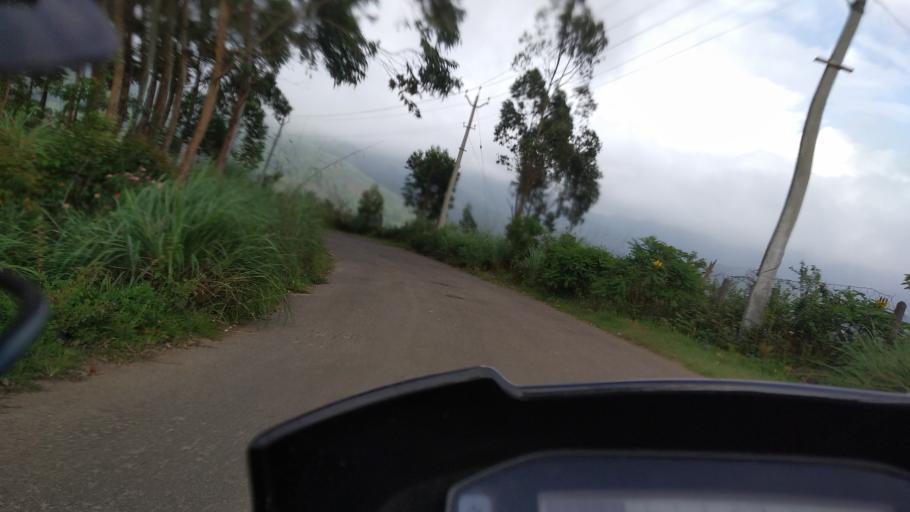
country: IN
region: Kerala
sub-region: Idukki
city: Munnar
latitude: 10.0385
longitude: 77.1817
